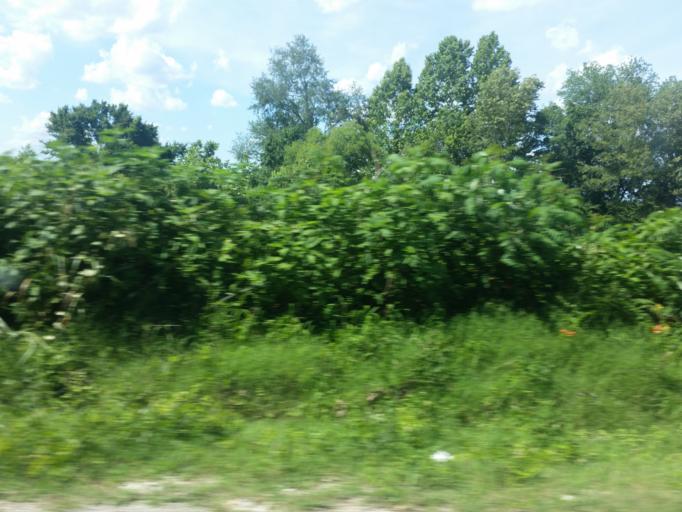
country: US
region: Tennessee
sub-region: Gibson County
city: Milan
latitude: 35.9732
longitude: -88.7119
